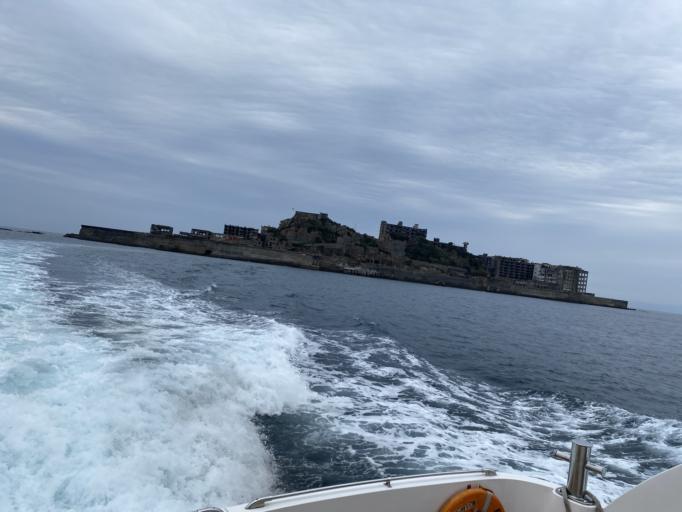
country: JP
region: Nagasaki
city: Nagasaki-shi
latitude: 32.6242
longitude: 129.7409
